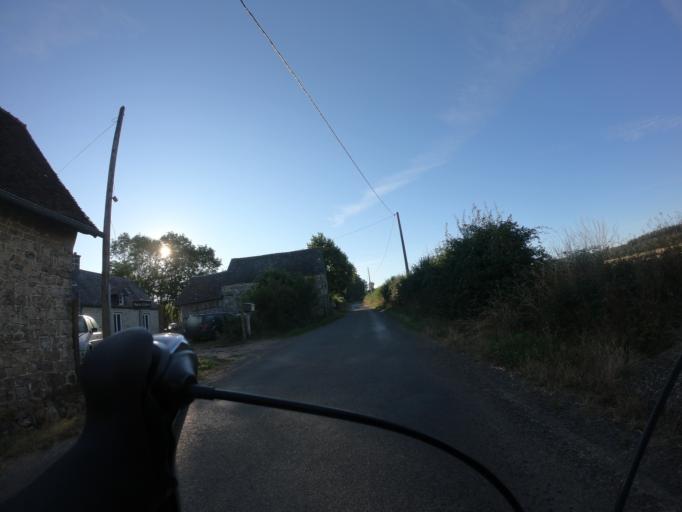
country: FR
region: Lower Normandy
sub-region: Departement de l'Orne
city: Magny-le-Desert
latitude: 48.5380
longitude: -0.2884
